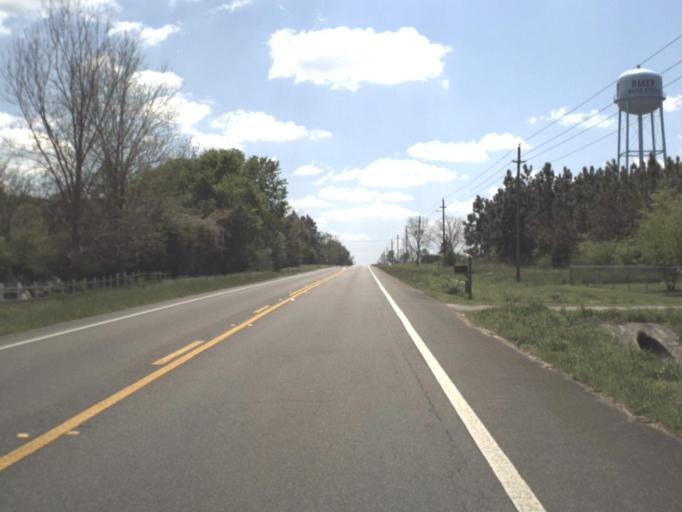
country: US
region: Florida
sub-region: Okaloosa County
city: Crestview
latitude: 30.8473
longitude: -86.6751
